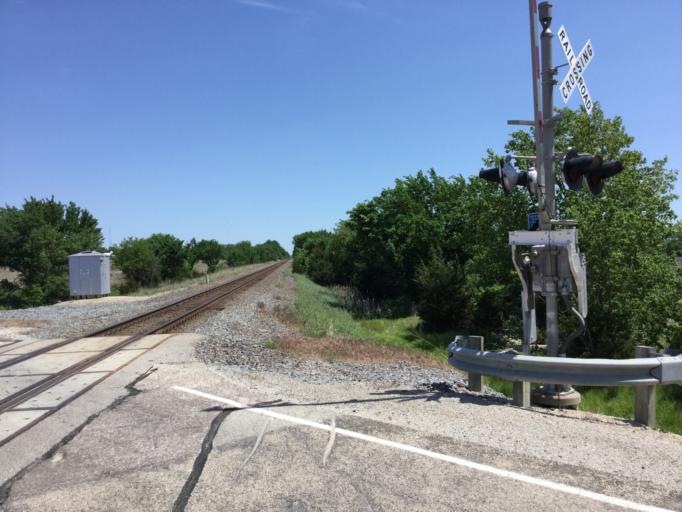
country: US
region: Kansas
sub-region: Coffey County
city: Burlington
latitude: 38.1479
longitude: -95.5550
